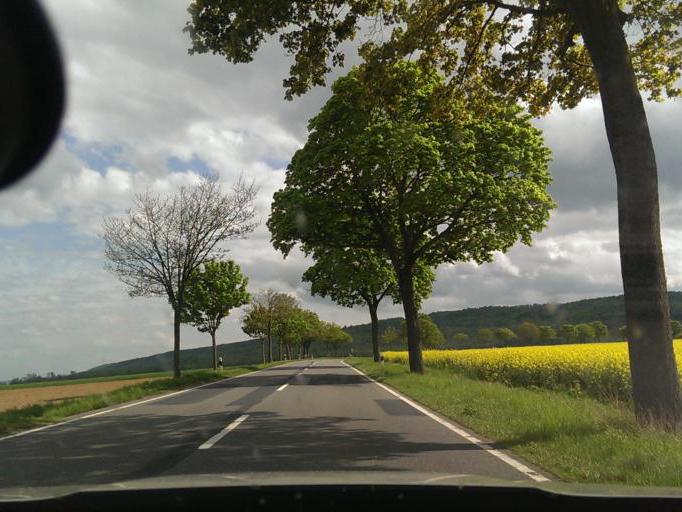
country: DE
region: Lower Saxony
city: Marienhagen
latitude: 52.0450
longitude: 9.6932
